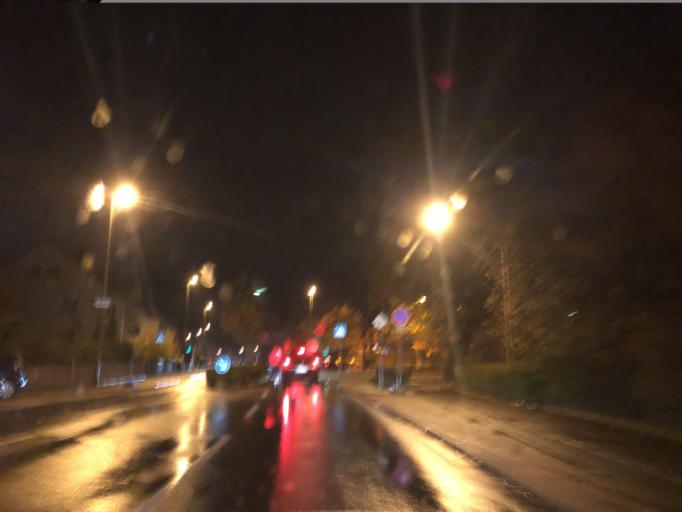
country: DE
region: Hesse
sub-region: Regierungsbezirk Darmstadt
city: Hochheim am Main
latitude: 50.0166
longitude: 8.3571
